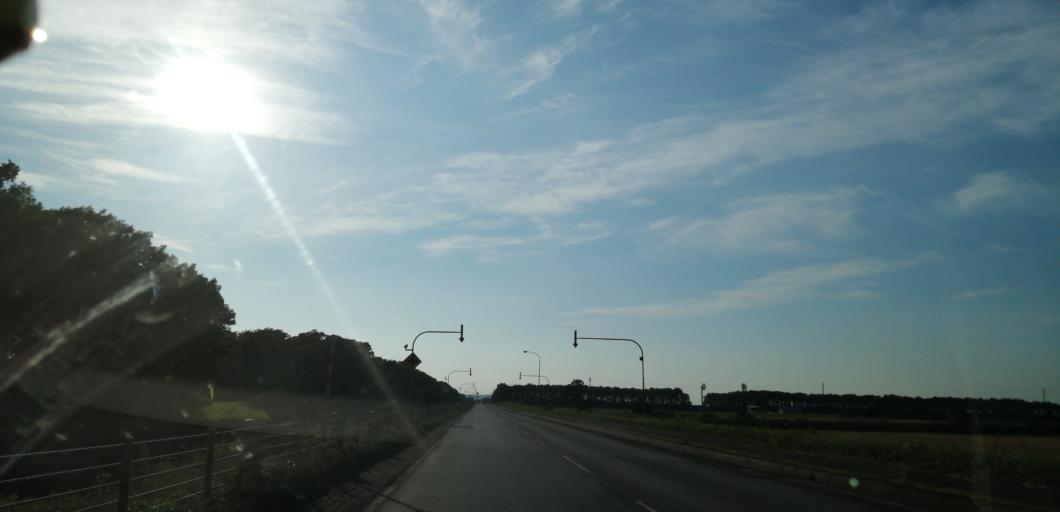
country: JP
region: Hokkaido
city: Kitahiroshima
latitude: 42.9755
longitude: 141.6484
